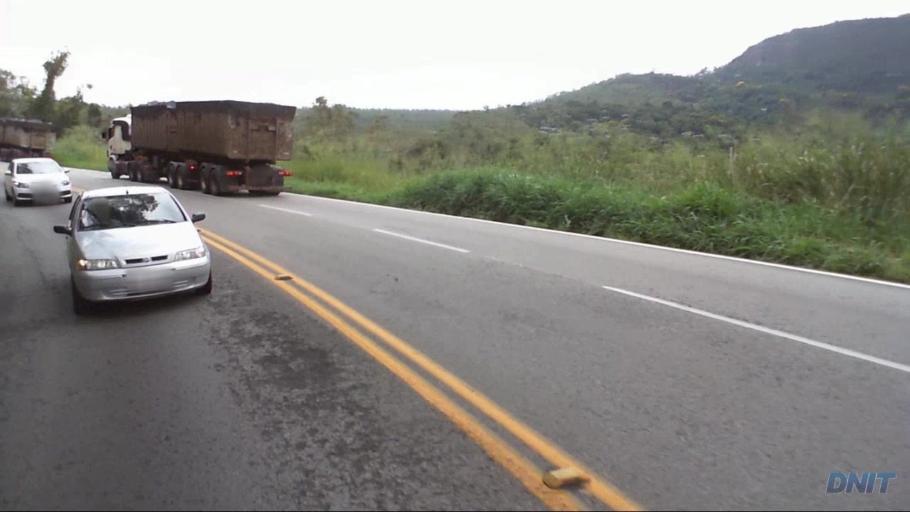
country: BR
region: Minas Gerais
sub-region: Joao Monlevade
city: Joao Monlevade
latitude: -19.8583
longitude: -43.1072
